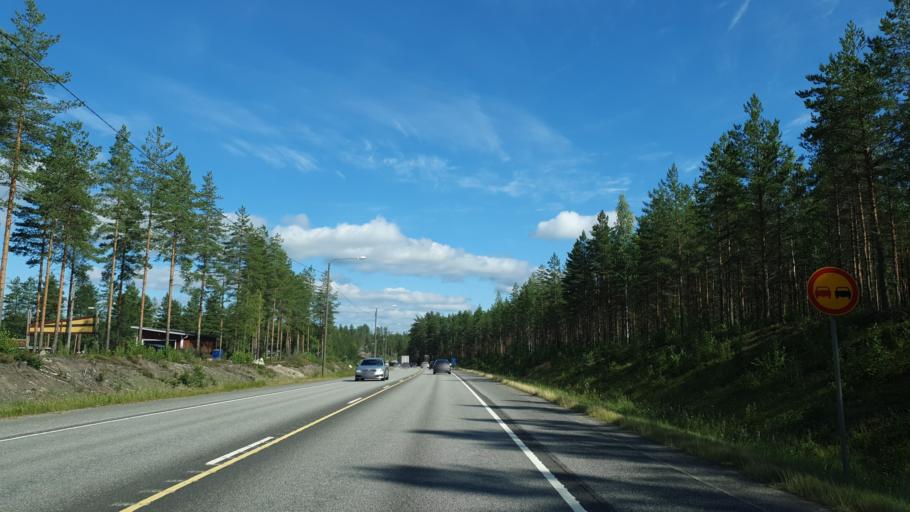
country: FI
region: Central Finland
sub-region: Jyvaeskylae
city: Toivakka
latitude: 62.2518
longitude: 26.1122
